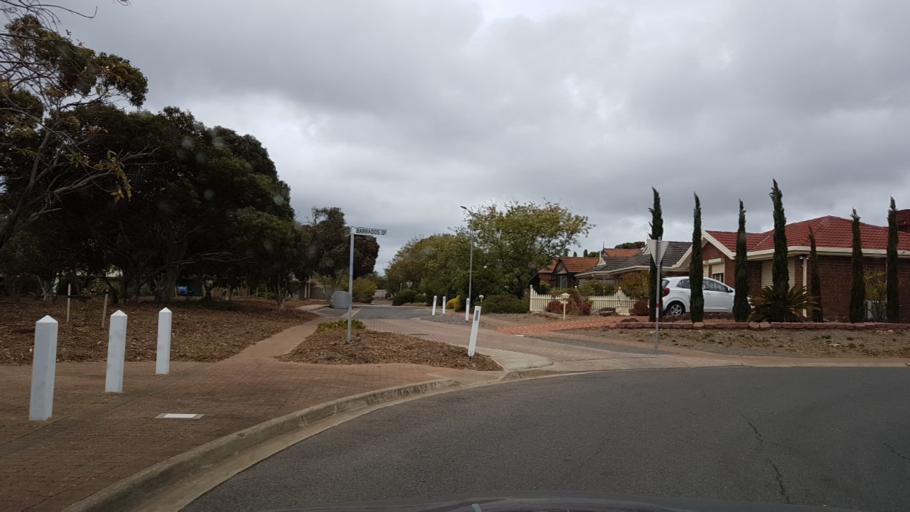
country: AU
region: South Australia
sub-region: Onkaparinga
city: Moana
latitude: -35.1955
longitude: 138.4888
